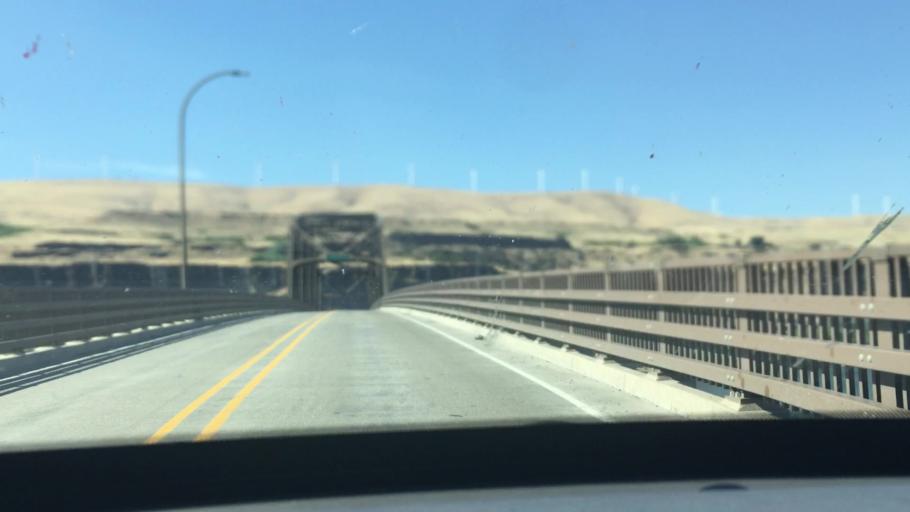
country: US
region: Washington
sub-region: Klickitat County
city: Goldendale
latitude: 45.6728
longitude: -120.8350
